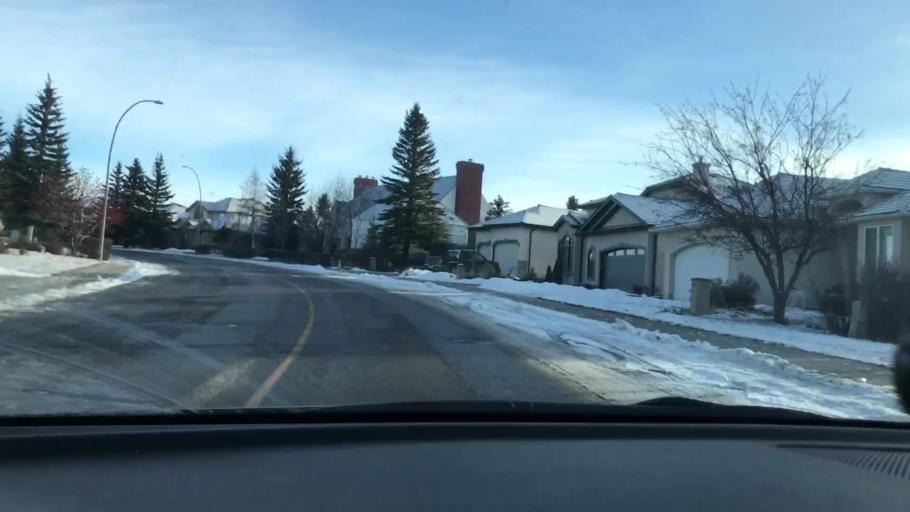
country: CA
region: Alberta
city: Calgary
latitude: 51.0221
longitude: -114.1767
